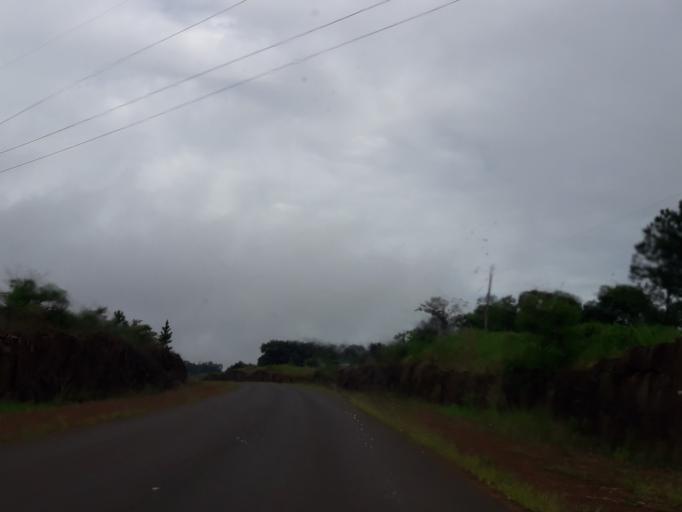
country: AR
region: Misiones
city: Bernardo de Irigoyen
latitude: -26.4290
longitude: -53.8507
